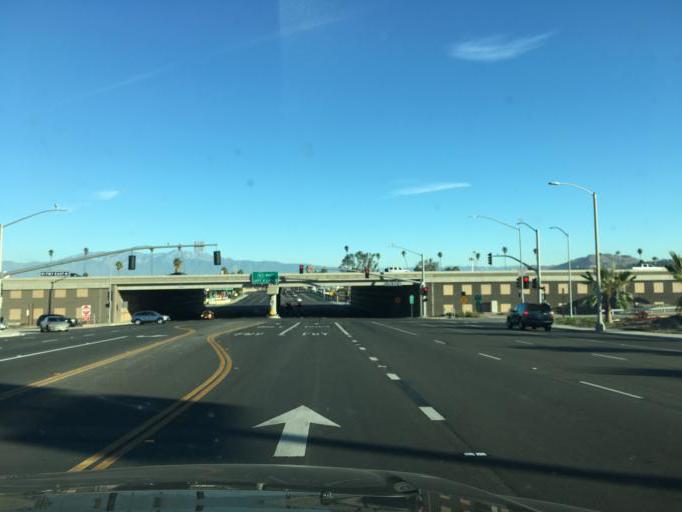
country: US
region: California
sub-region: Riverside County
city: Corona
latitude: 33.8788
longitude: -117.5659
